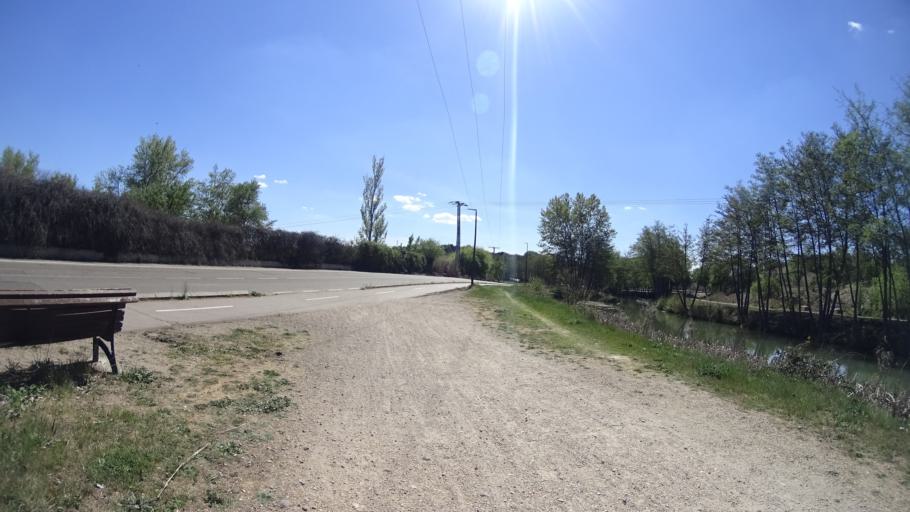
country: ES
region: Castille and Leon
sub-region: Provincia de Valladolid
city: Santovenia de Pisuerga
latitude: 41.6899
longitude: -4.7173
